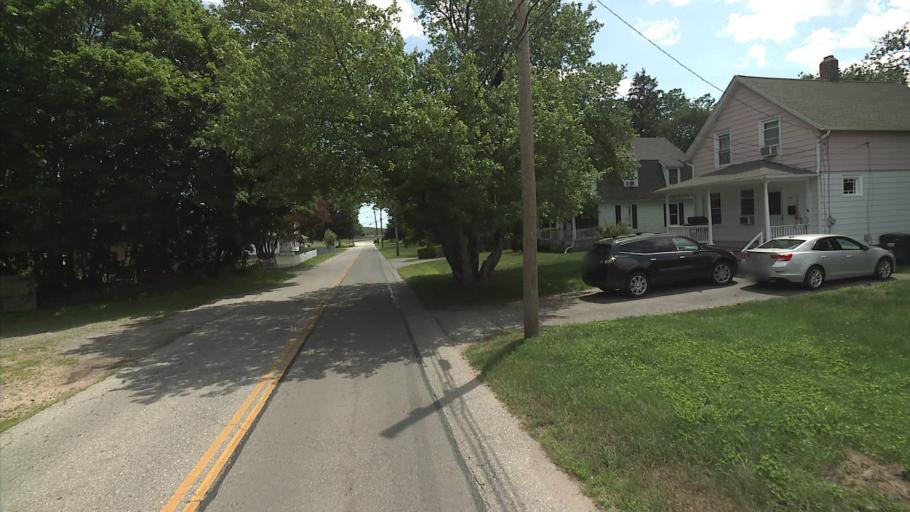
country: US
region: Connecticut
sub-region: New London County
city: Poquonock Bridge
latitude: 41.3404
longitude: -72.0388
